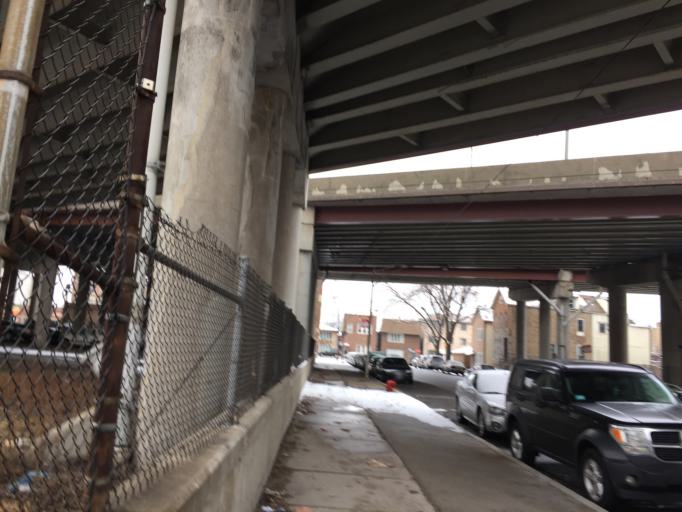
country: US
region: Illinois
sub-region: Cook County
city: Chicago
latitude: 41.8445
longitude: -87.6332
